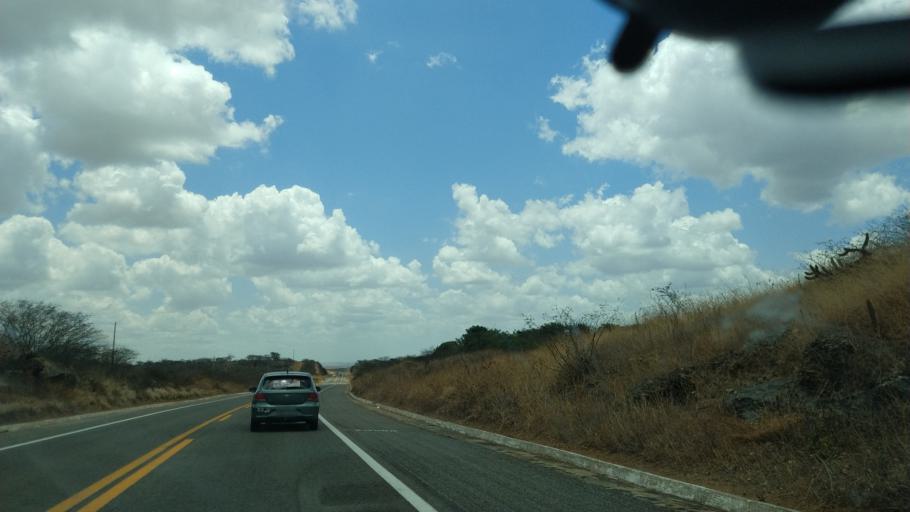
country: BR
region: Rio Grande do Norte
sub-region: Cerro Cora
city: Cerro Cora
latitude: -6.2109
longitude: -36.3025
